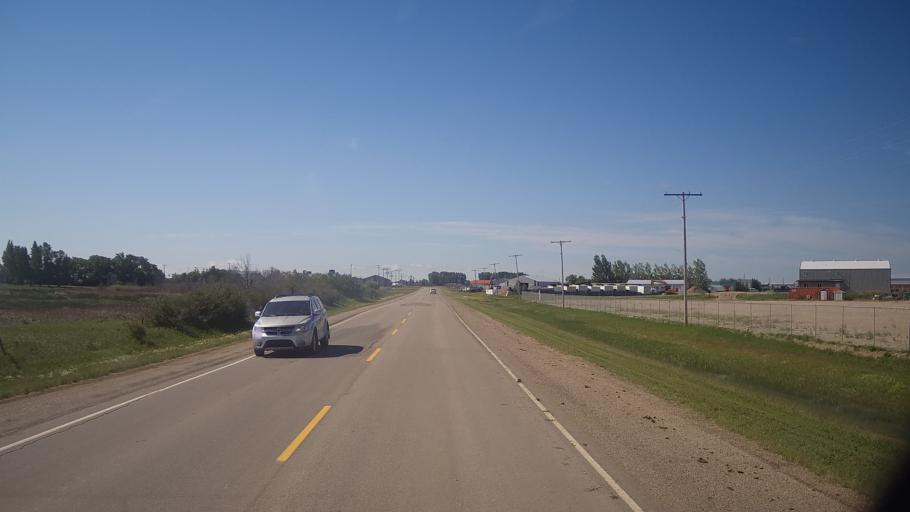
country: CA
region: Saskatchewan
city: Watrous
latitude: 51.6738
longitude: -105.4518
